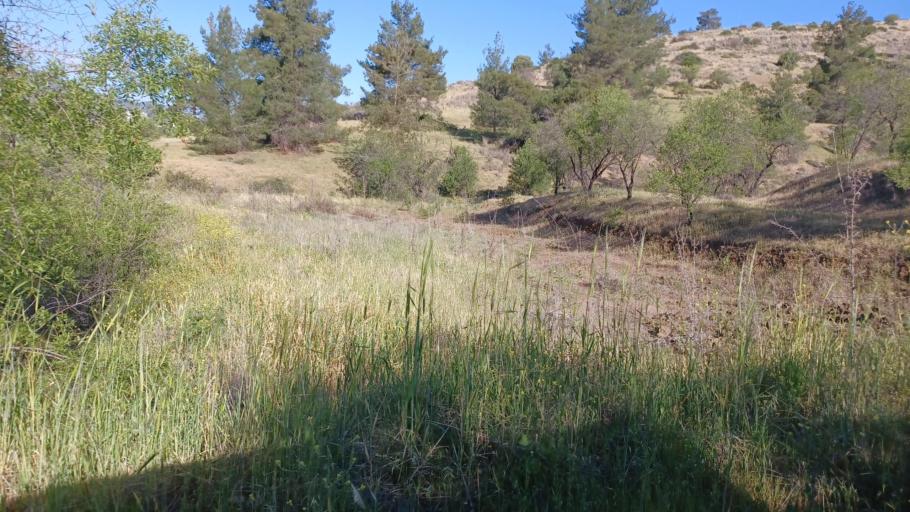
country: CY
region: Lefkosia
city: Peristerona
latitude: 35.0236
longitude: 33.0524
